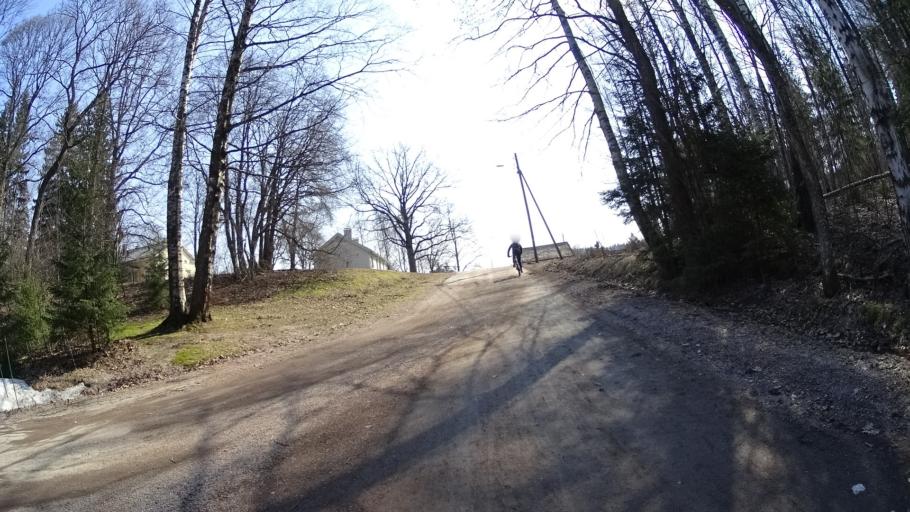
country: FI
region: Uusimaa
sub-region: Helsinki
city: Espoo
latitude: 60.2092
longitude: 24.6471
